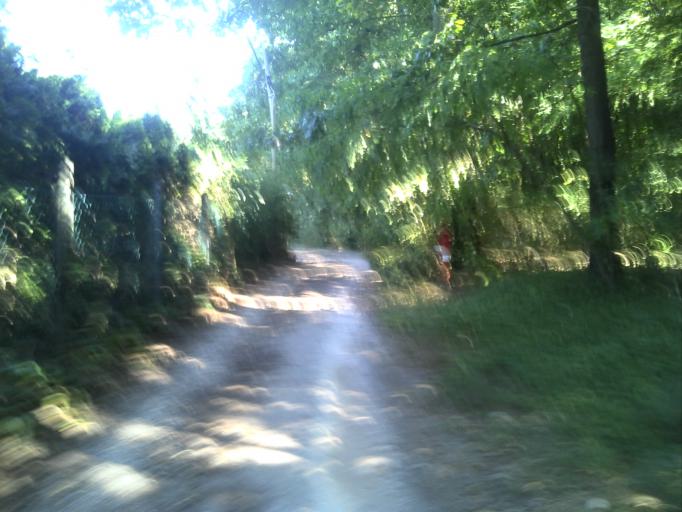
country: HU
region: Pest
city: Piliscsaba
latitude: 47.6360
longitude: 18.8534
